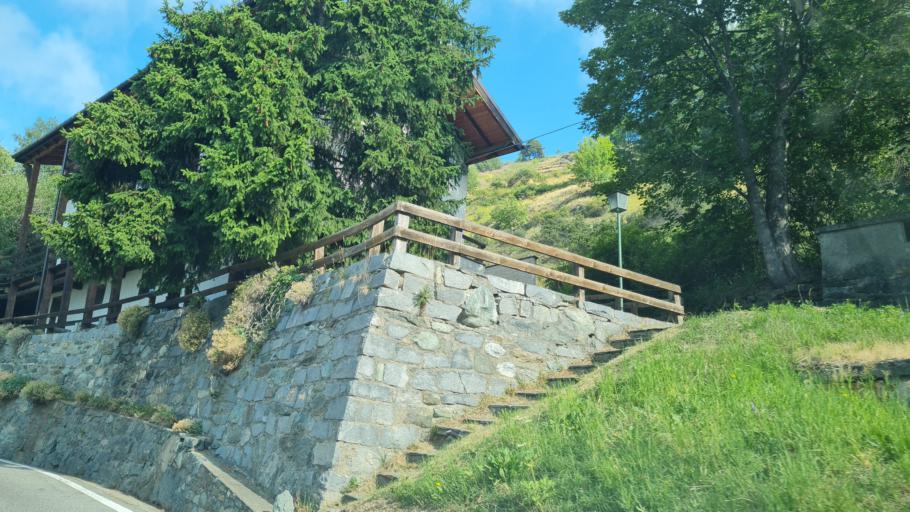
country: IT
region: Aosta Valley
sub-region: Valle d'Aosta
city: La Magdeleine
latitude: 45.8141
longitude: 7.6140
